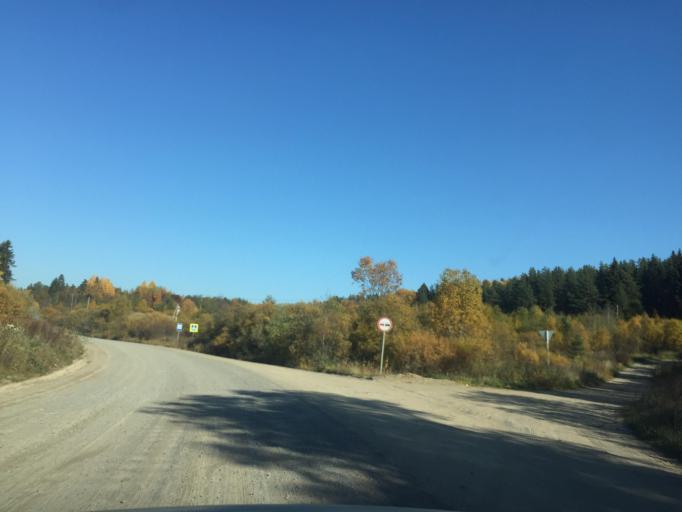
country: RU
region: Leningrad
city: Kuznechnoye
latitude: 61.3121
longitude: 29.9421
